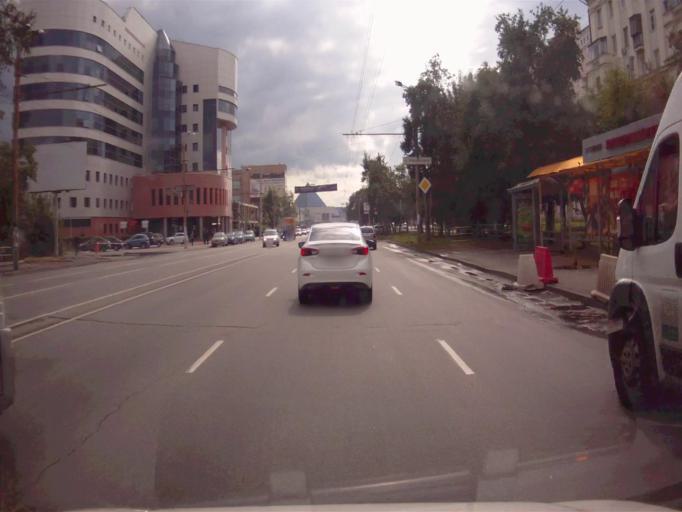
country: RU
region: Chelyabinsk
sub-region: Gorod Chelyabinsk
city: Chelyabinsk
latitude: 55.1453
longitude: 61.4161
